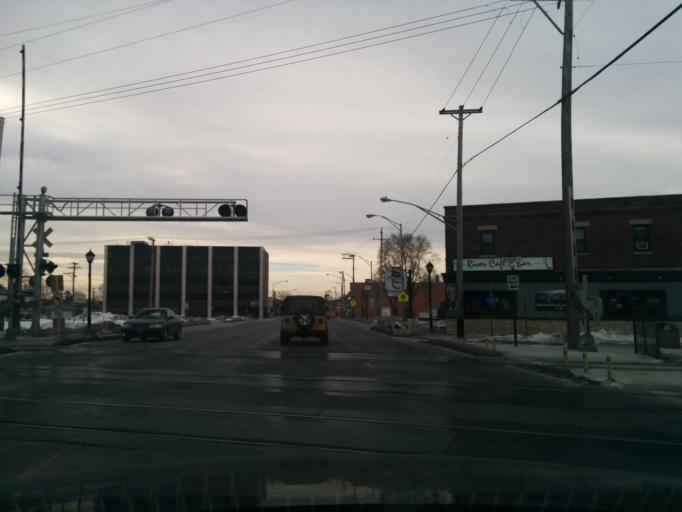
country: US
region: Illinois
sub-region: Cook County
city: River Grove
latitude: 41.9310
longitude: -87.8358
